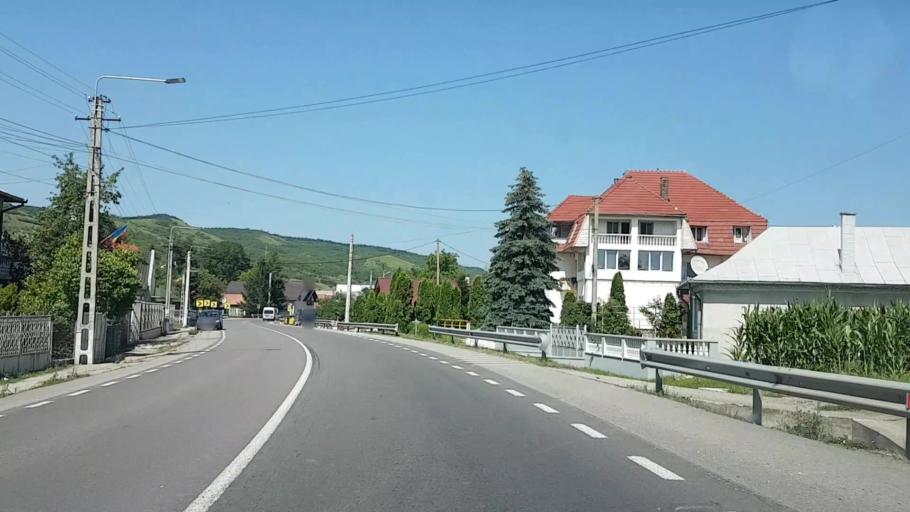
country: RO
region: Bistrita-Nasaud
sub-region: Comuna Petru Rares
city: Reteag
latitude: 47.1934
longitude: 24.0141
